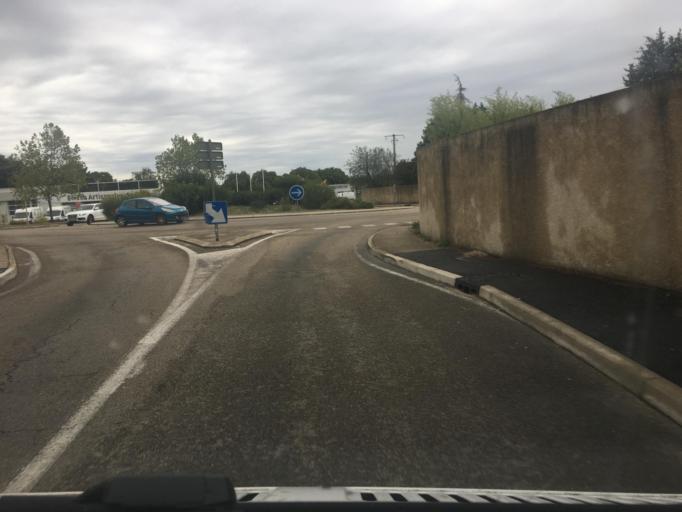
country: FR
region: Languedoc-Roussillon
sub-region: Departement du Gard
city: Uzes
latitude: 44.0200
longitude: 4.4018
